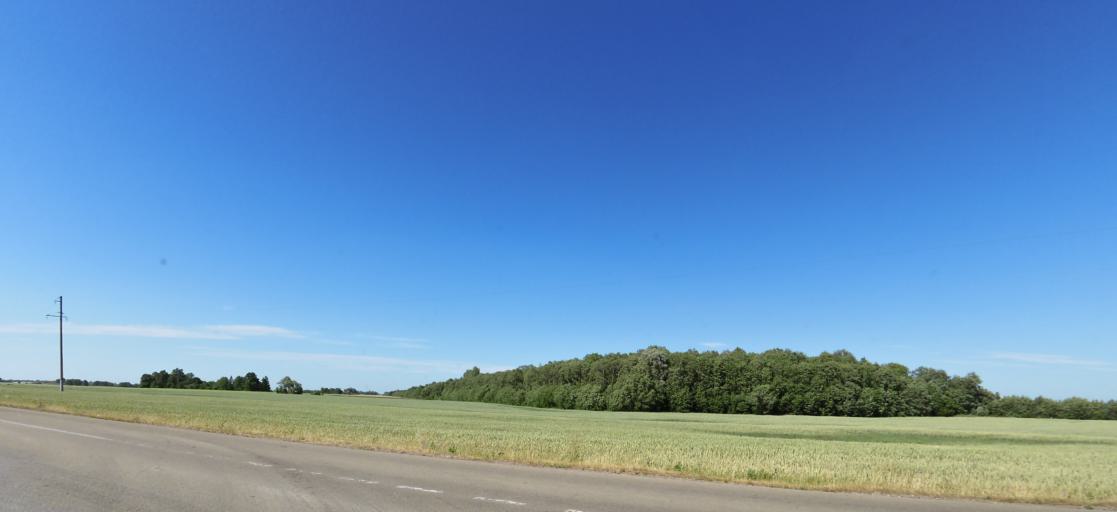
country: LT
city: Vabalninkas
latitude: 55.9991
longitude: 24.6694
